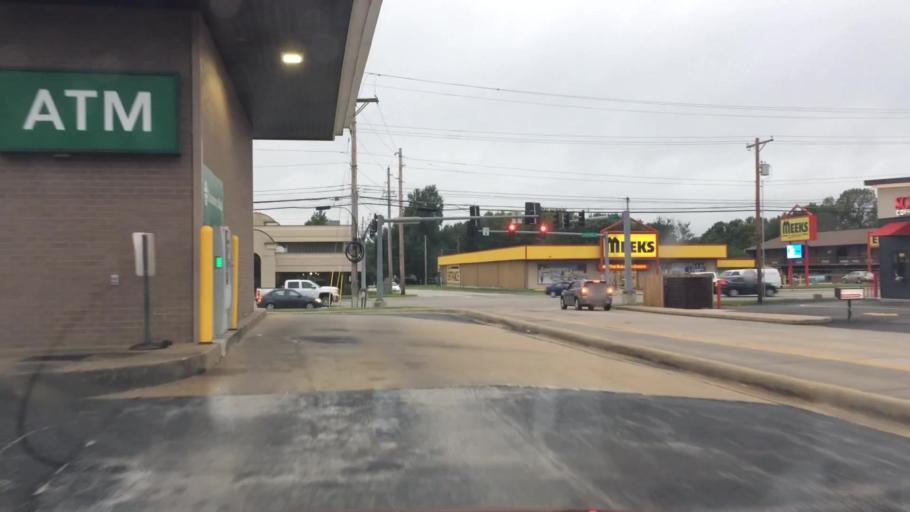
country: US
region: Missouri
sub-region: Greene County
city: Springfield
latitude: 37.1814
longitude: -93.2281
